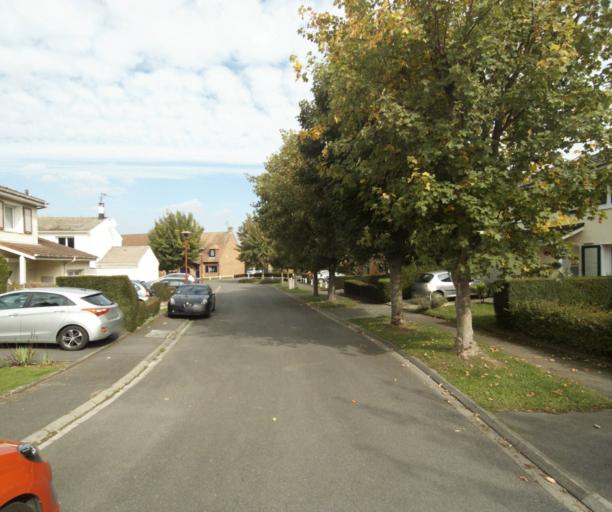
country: FR
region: Nord-Pas-de-Calais
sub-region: Departement du Nord
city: Templemars
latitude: 50.5728
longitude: 3.0590
